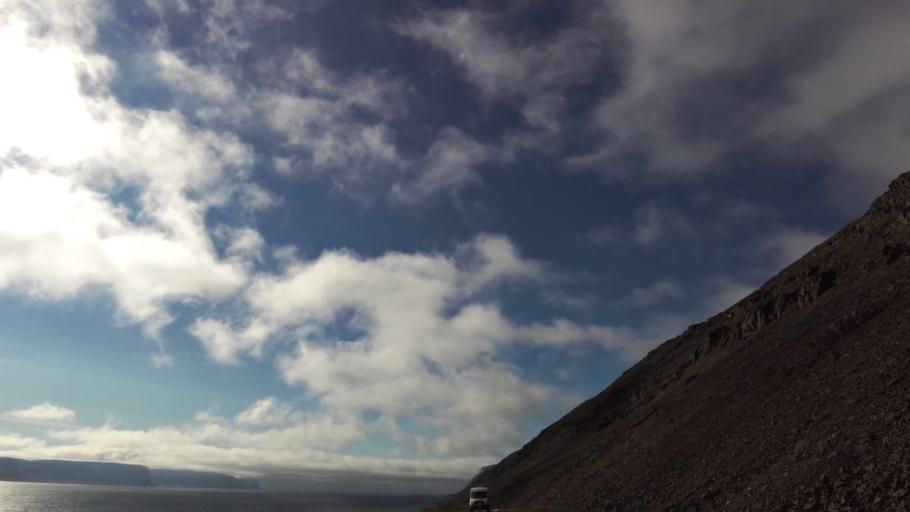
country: IS
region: West
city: Olafsvik
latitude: 65.5590
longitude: -23.9054
